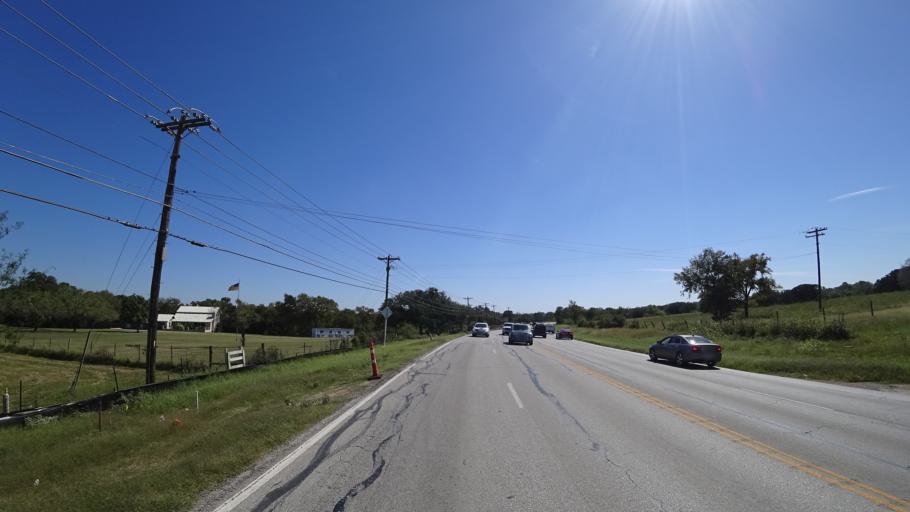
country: US
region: Texas
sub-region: Travis County
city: Hornsby Bend
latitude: 30.2705
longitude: -97.6294
